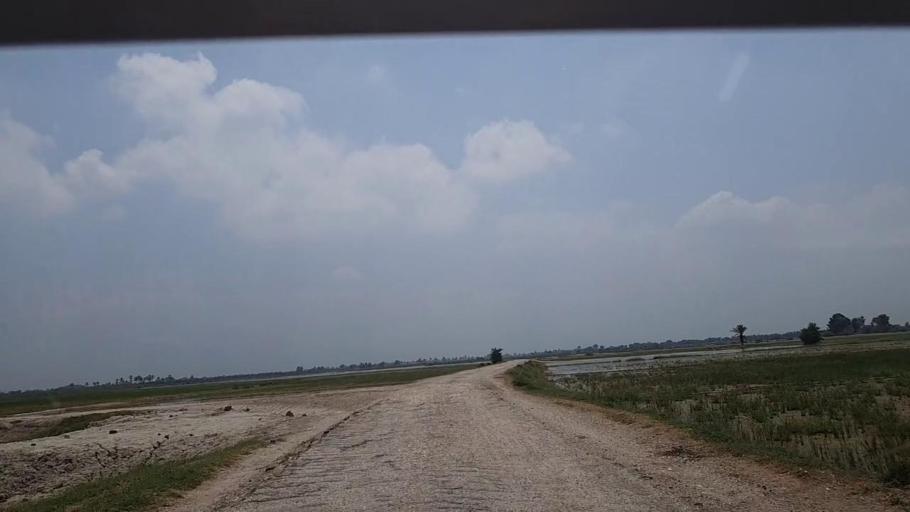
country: PK
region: Sindh
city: Khanpur
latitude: 27.9005
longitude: 69.3909
